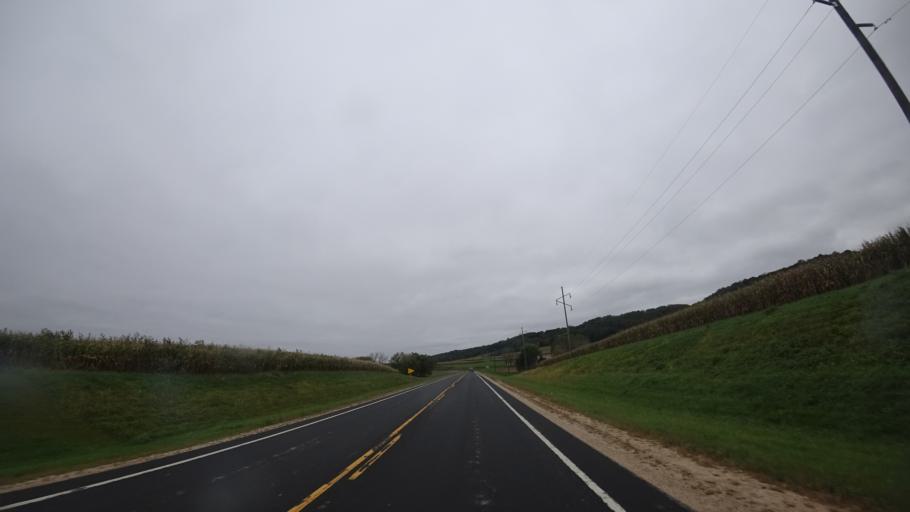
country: US
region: Wisconsin
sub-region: Grant County
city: Boscobel
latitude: 43.1048
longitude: -90.8190
